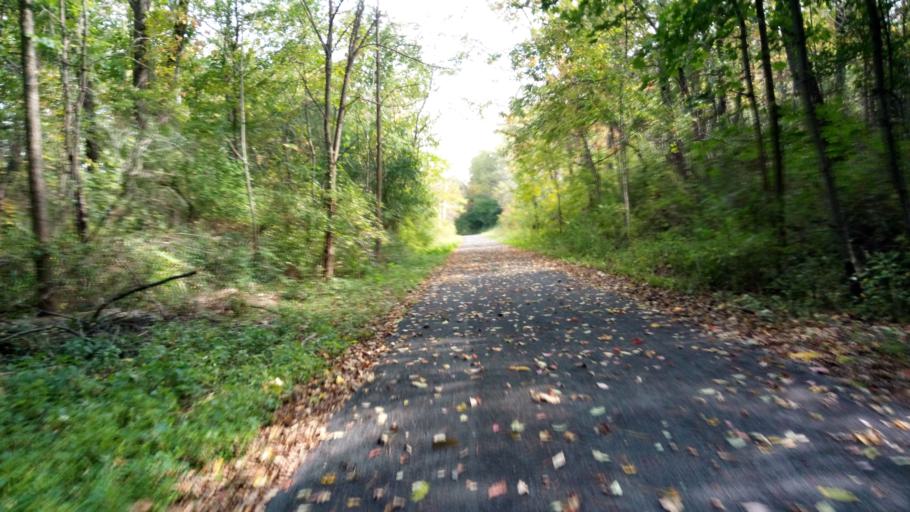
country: US
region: New York
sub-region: Wayne County
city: Clyde
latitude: 43.0668
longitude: -76.8507
